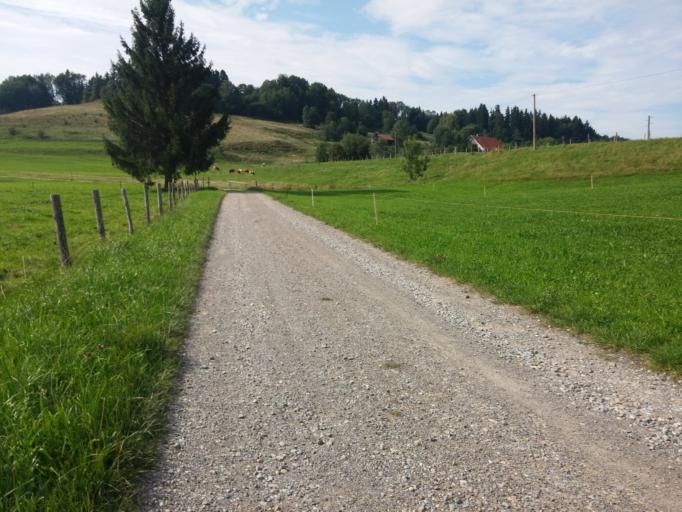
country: DE
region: Bavaria
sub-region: Swabia
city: Woringen
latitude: 47.8676
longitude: 10.2018
